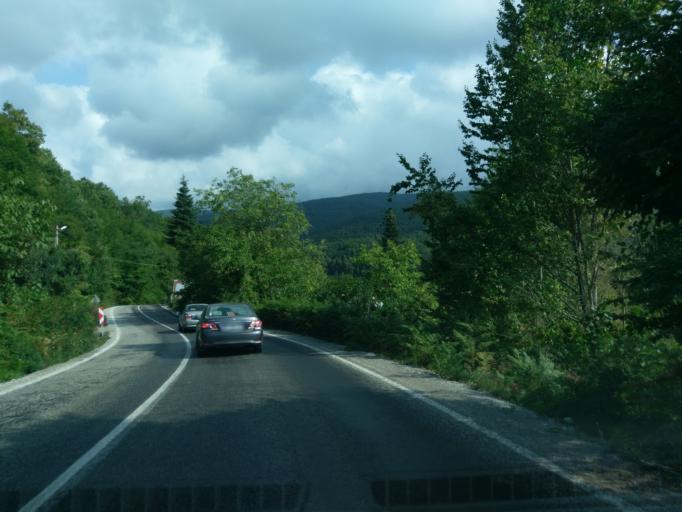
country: TR
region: Sinop
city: Ayancik
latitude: 41.8792
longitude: 34.5207
